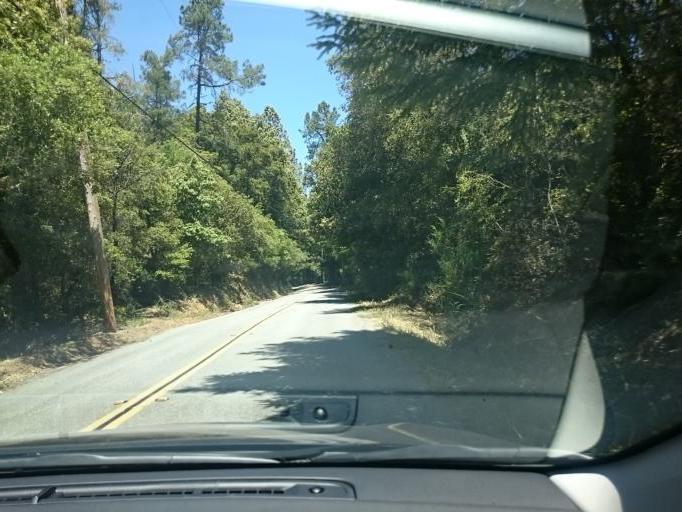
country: US
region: California
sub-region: Santa Cruz County
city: Bonny Doon
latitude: 37.0587
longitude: -122.1262
